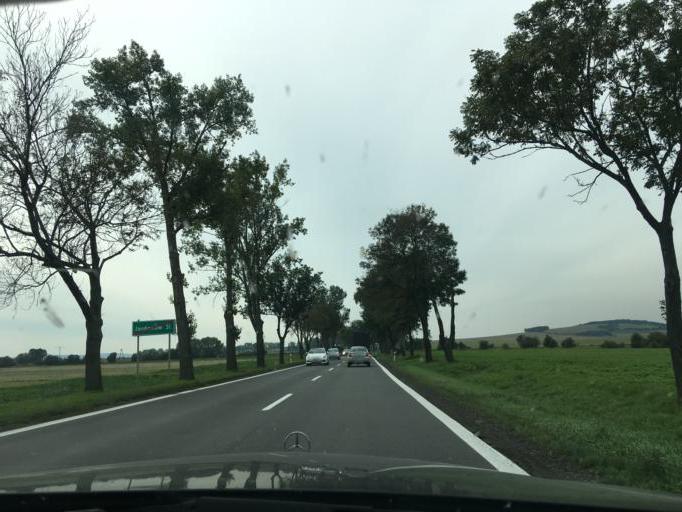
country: PL
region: Lower Silesian Voivodeship
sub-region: Powiat wroclawski
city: Jordanow Slaski
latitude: 50.8518
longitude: 16.8645
